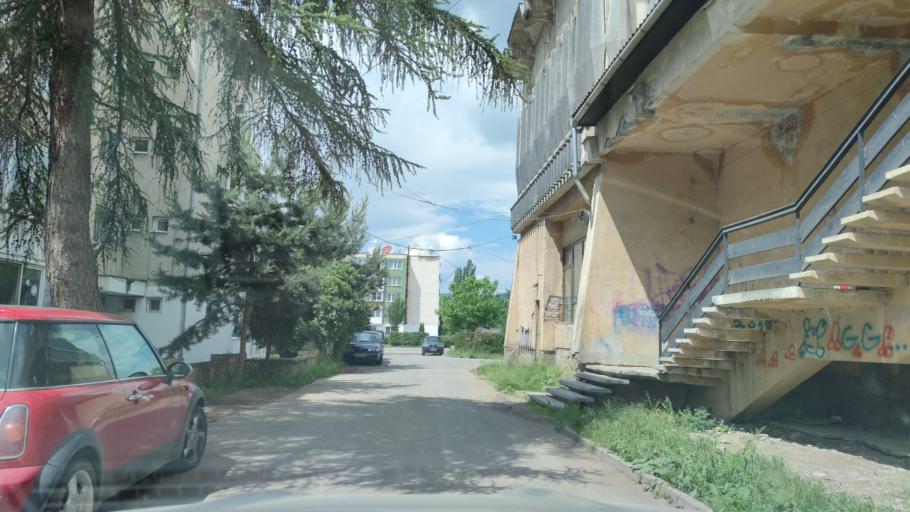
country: RO
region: Harghita
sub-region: Municipiul Gheorgheni
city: Gheorgheni
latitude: 46.7221
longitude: 25.5950
